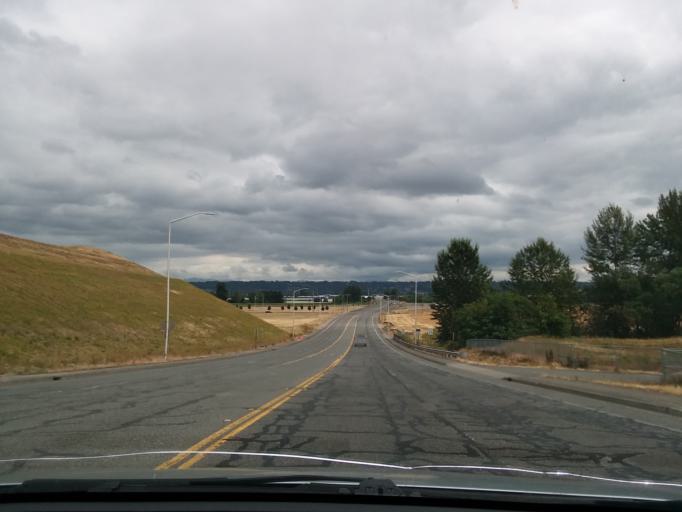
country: US
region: Washington
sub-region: King County
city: SeaTac
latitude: 47.4229
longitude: -122.2764
